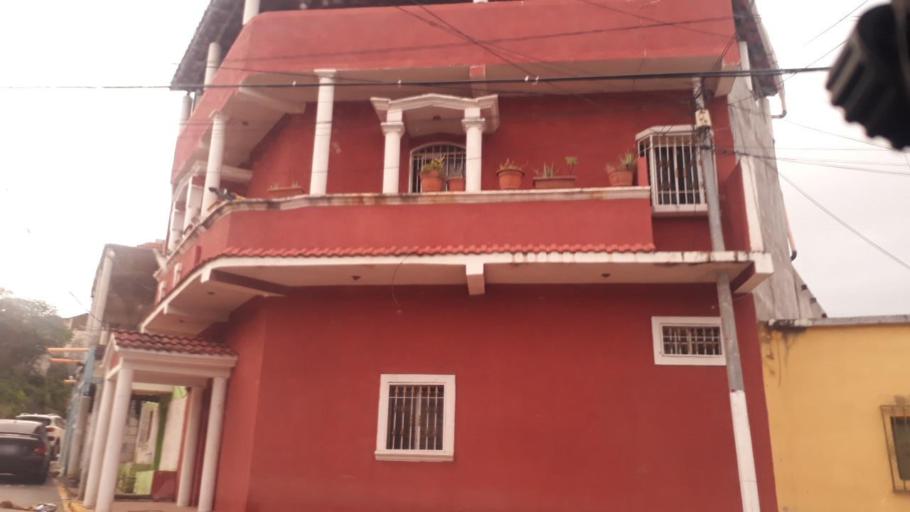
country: GT
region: Jutiapa
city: Jutiapa
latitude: 14.2887
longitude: -89.8970
